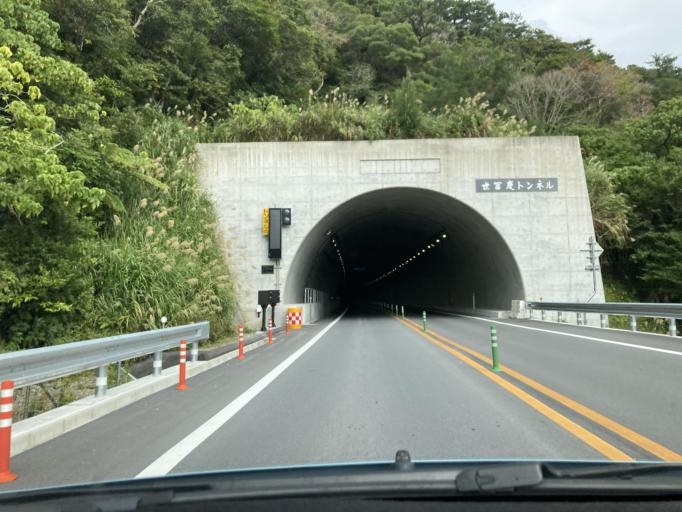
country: JP
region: Okinawa
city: Nago
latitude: 26.5668
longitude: 127.9870
